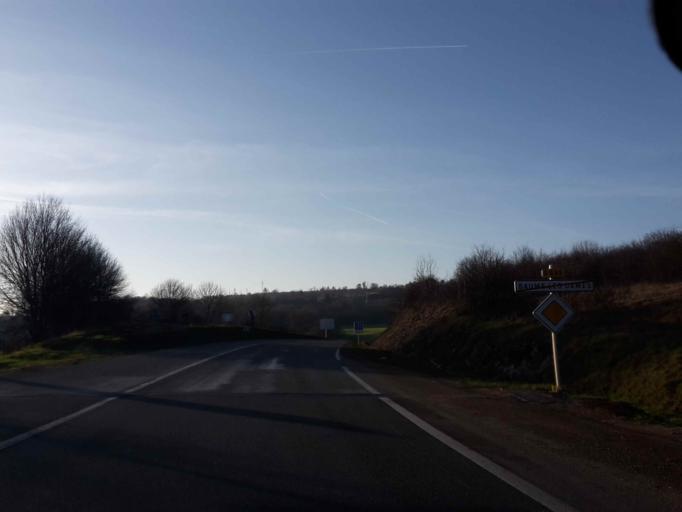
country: FR
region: Franche-Comte
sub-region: Departement du Doubs
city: Baume-les-Dames
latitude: 47.3490
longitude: 6.3359
